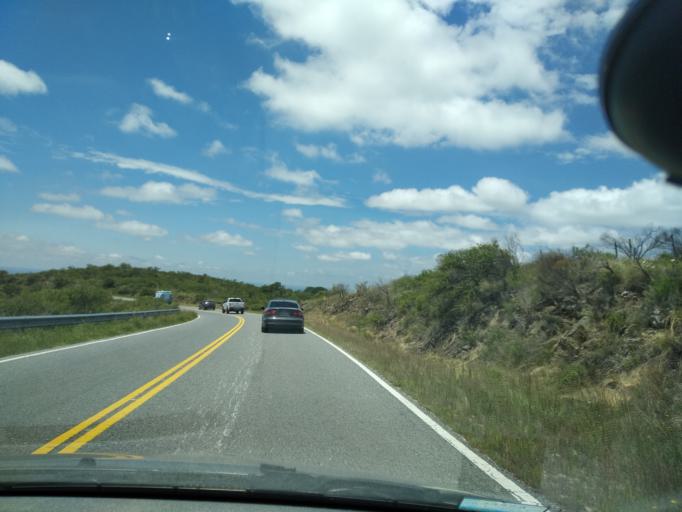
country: AR
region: Cordoba
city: Alta Gracia
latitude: -31.5931
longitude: -64.5259
